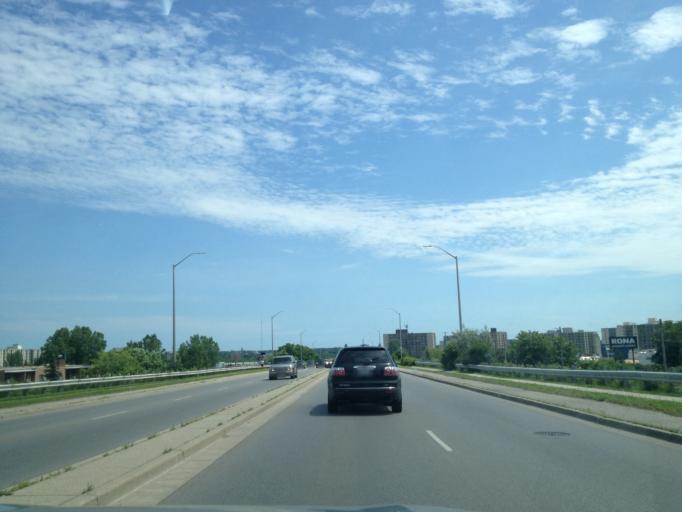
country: CA
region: Ontario
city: London
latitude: 42.9941
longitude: -81.2980
